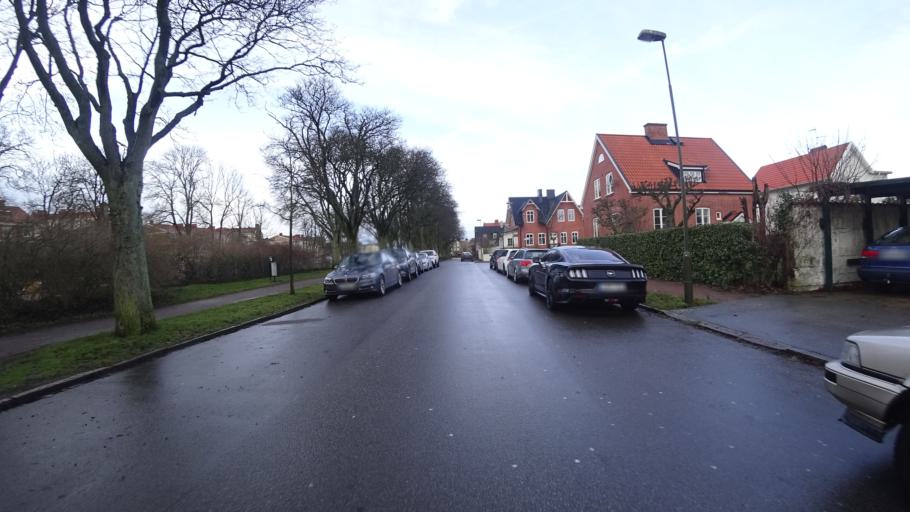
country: SE
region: Skane
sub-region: Malmo
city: Bunkeflostrand
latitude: 55.5786
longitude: 12.9366
